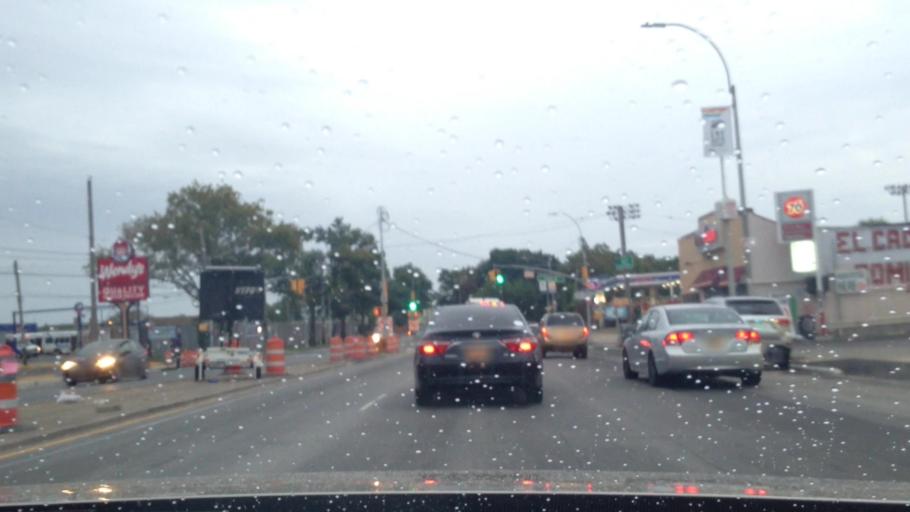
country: US
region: New York
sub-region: Kings County
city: East New York
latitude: 40.6798
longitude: -73.8783
